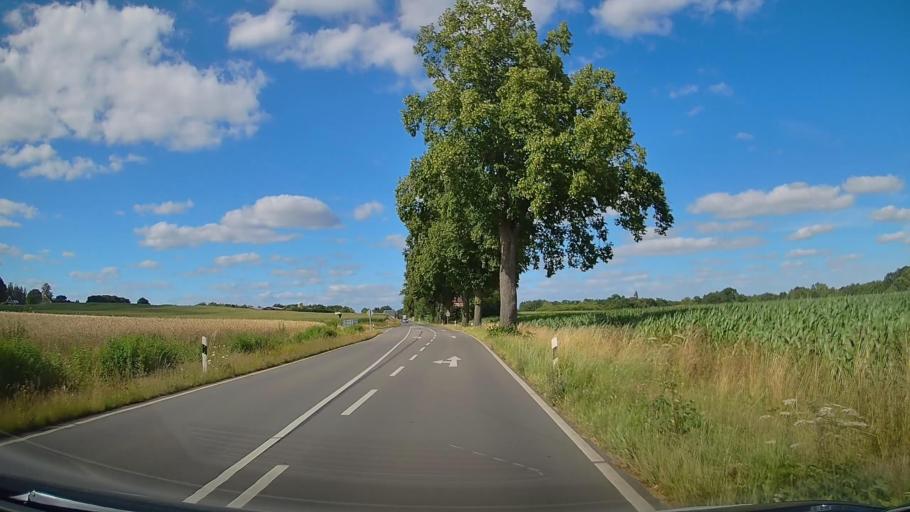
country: DE
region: Lower Saxony
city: Bippen
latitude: 52.6086
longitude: 7.7439
